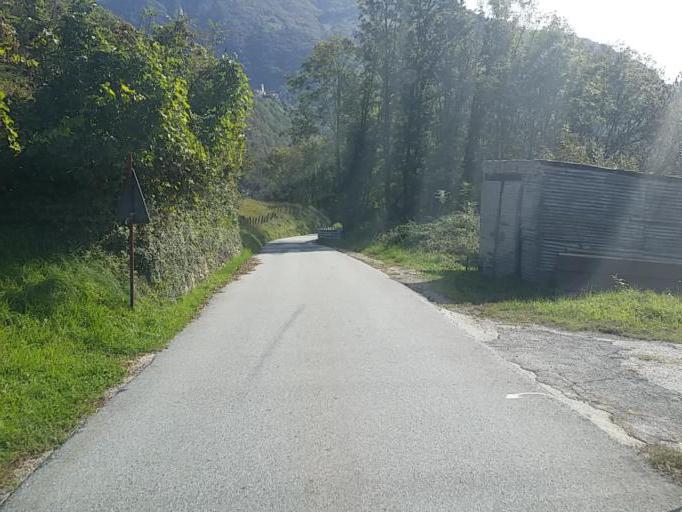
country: IT
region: Piedmont
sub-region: Provincia Verbano-Cusio-Ossola
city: Cursolo
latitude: 46.0944
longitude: 8.5835
